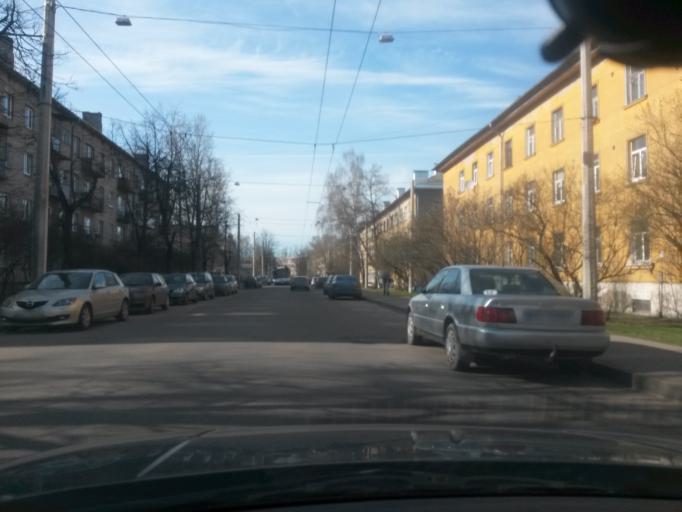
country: LV
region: Kekava
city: Balozi
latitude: 56.9104
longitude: 24.1943
